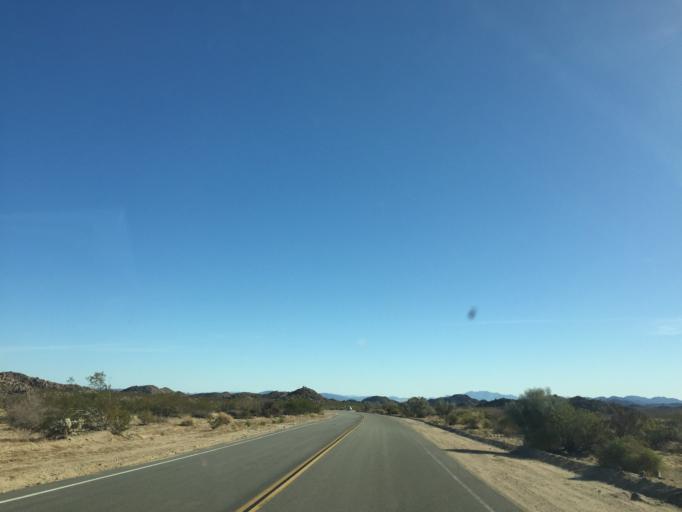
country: US
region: California
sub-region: Riverside County
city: Mecca
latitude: 33.8032
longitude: -115.7794
